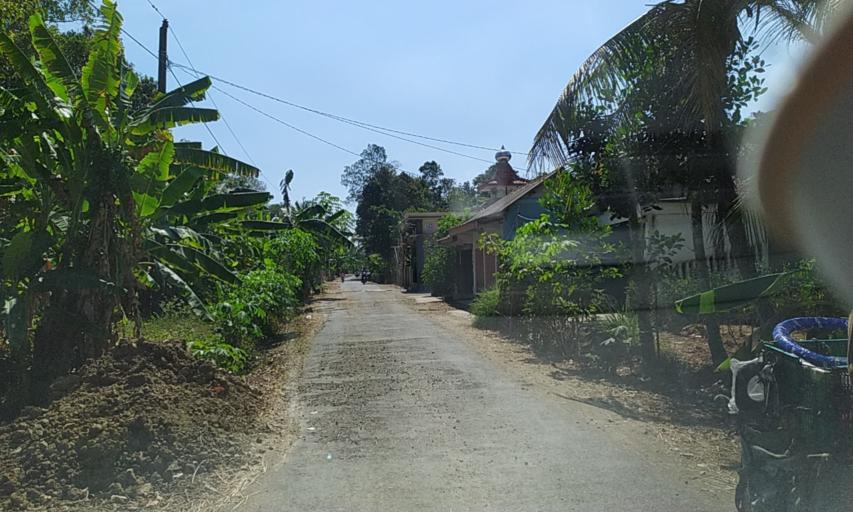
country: ID
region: Central Java
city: Kroya
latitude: -7.6772
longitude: 109.3379
